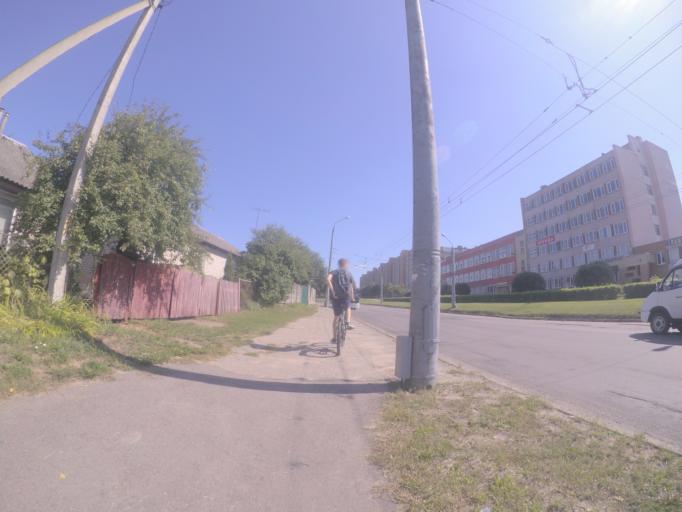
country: BY
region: Grodnenskaya
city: Hrodna
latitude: 53.6637
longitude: 23.7954
